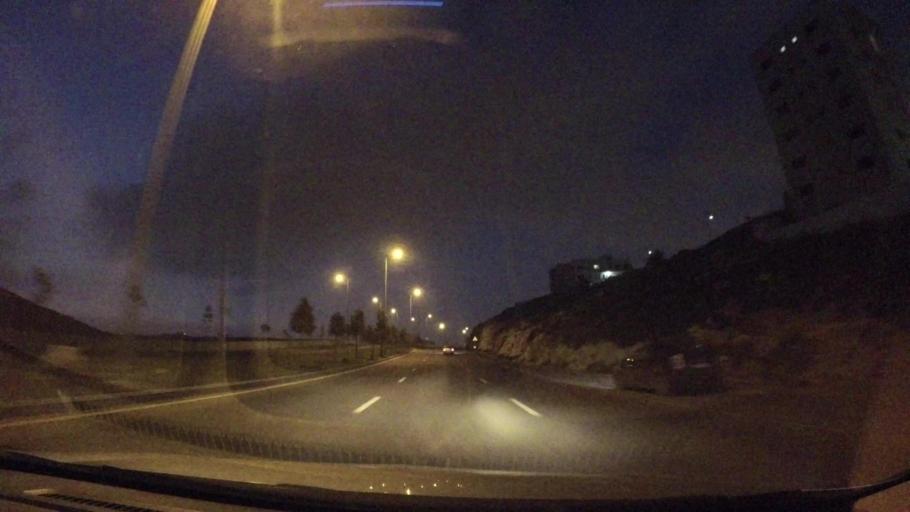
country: JO
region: Amman
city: Al Bunayyat ash Shamaliyah
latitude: 31.9220
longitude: 35.8789
